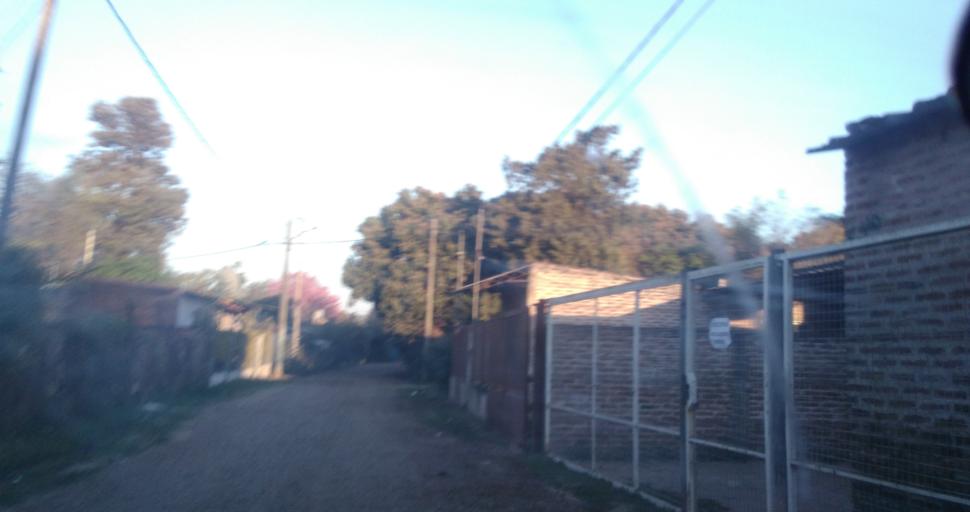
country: AR
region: Chaco
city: Fontana
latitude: -27.4282
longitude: -59.0187
